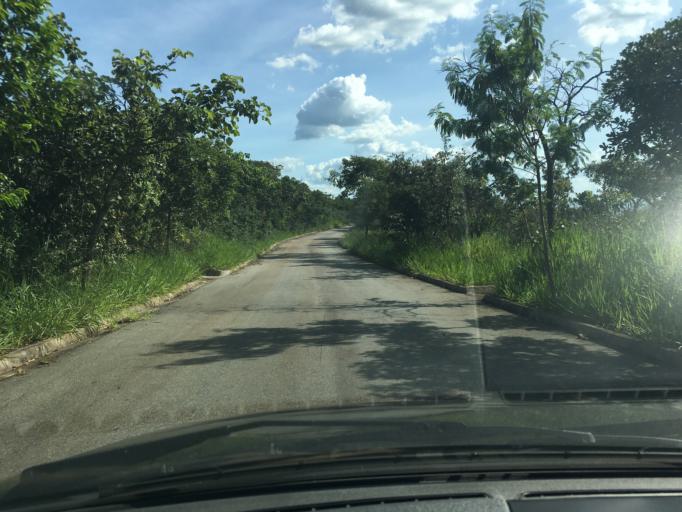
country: BR
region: Minas Gerais
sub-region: Ibirite
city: Ibirite
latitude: -20.1263
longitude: -44.0684
